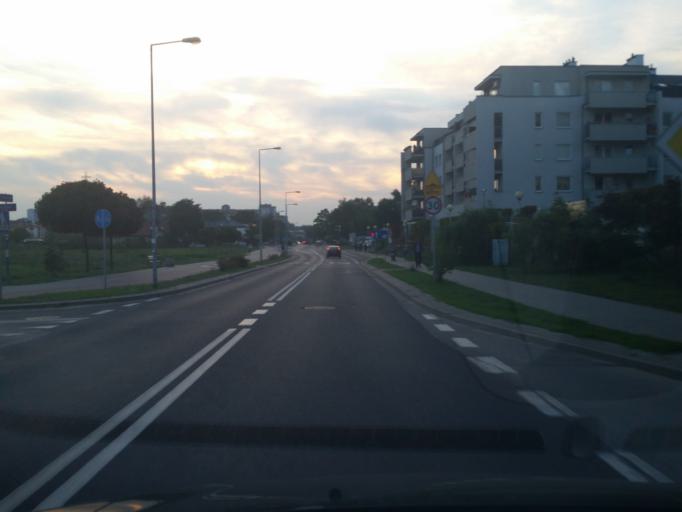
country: PL
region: Masovian Voivodeship
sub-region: Warszawa
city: Bialoleka
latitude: 52.3319
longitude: 20.9515
